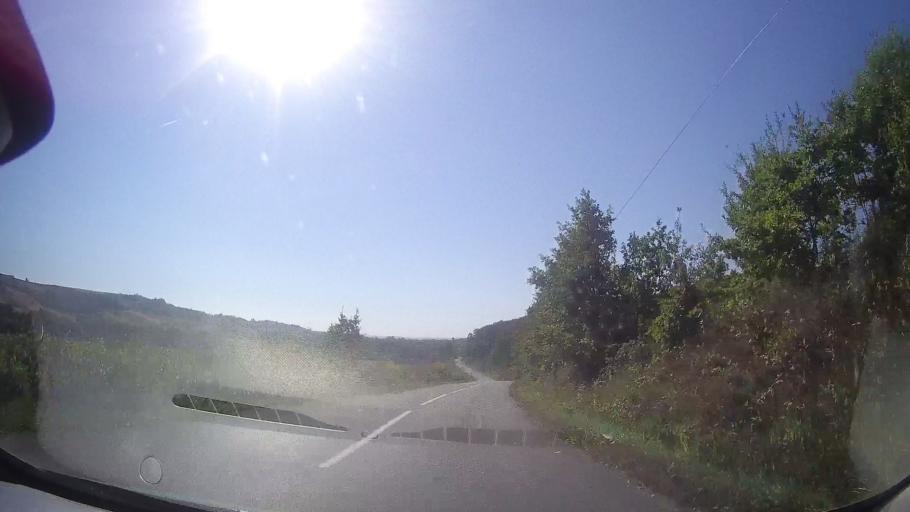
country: RO
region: Timis
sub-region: Comuna Ohaba Lunga
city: Ohaba Lunga
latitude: 45.8921
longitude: 21.9704
